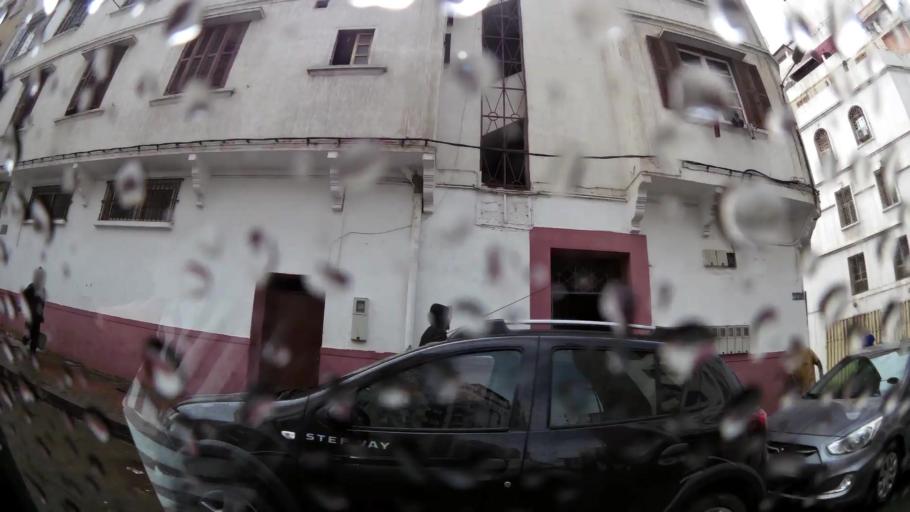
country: MA
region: Grand Casablanca
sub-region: Casablanca
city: Casablanca
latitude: 33.5698
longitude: -7.5954
